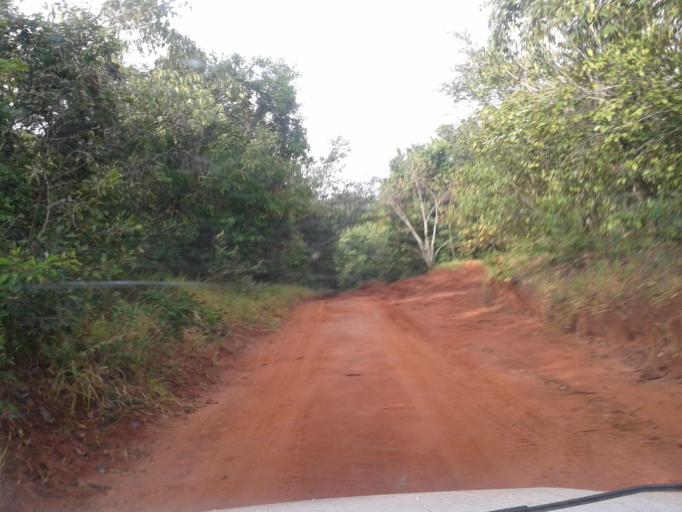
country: BR
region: Minas Gerais
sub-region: Campina Verde
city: Campina Verde
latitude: -19.4048
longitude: -49.6342
